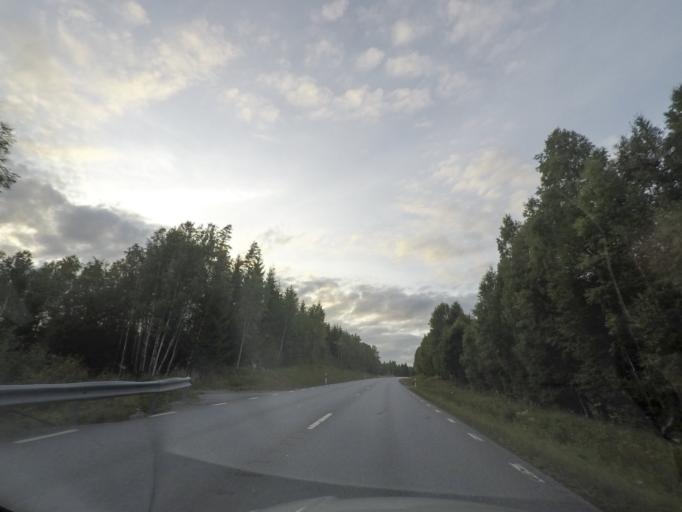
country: SE
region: OErebro
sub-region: Hallefors Kommun
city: Haellefors
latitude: 59.6527
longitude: 14.5806
